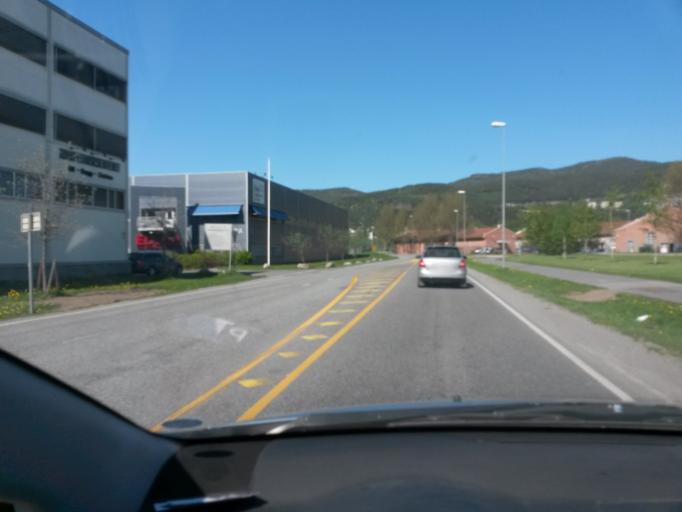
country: NO
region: Buskerud
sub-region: Nedre Eiker
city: Mjondalen
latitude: 59.7487
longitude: 10.0273
